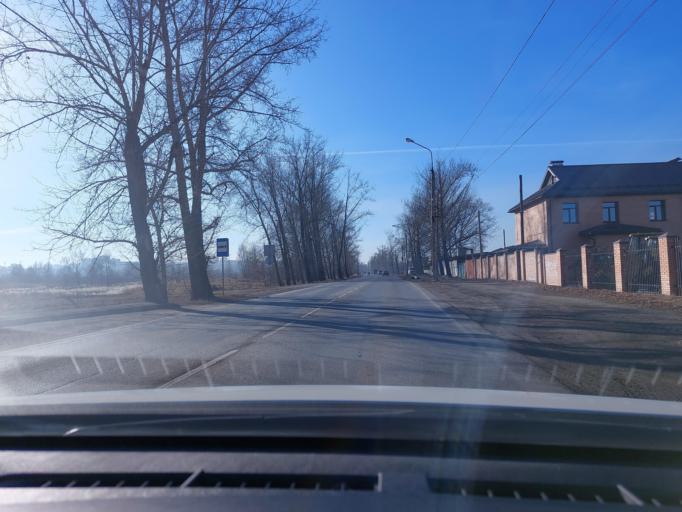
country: RU
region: Irkutsk
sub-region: Irkutskiy Rayon
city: Irkutsk
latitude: 52.3065
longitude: 104.2555
